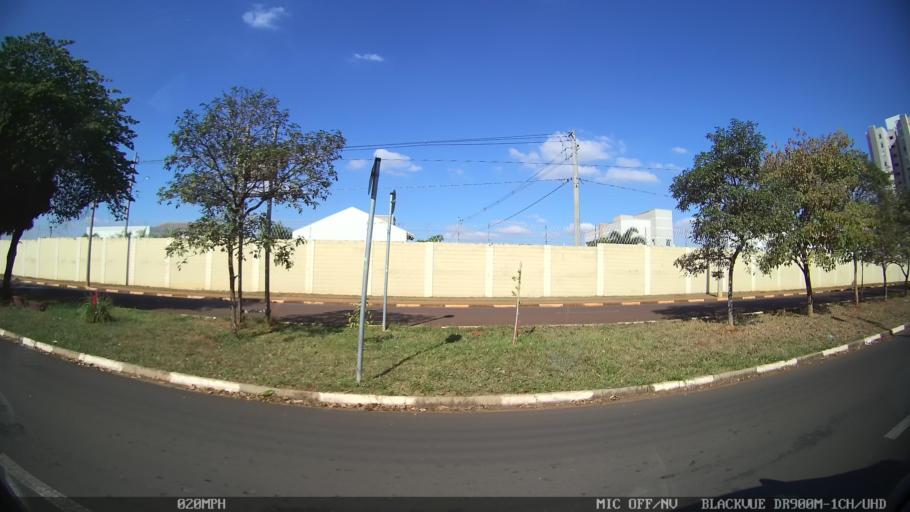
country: BR
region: Sao Paulo
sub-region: Sumare
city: Sumare
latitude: -22.8204
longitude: -47.2896
